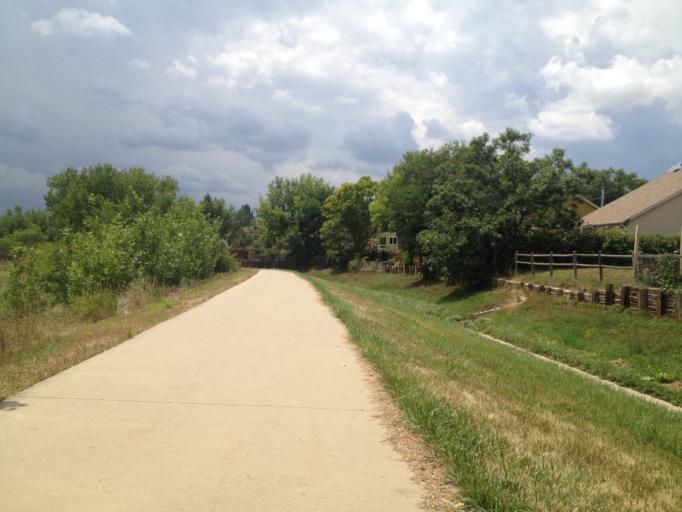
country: US
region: Colorado
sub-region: Boulder County
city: Louisville
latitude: 39.9687
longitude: -105.1484
